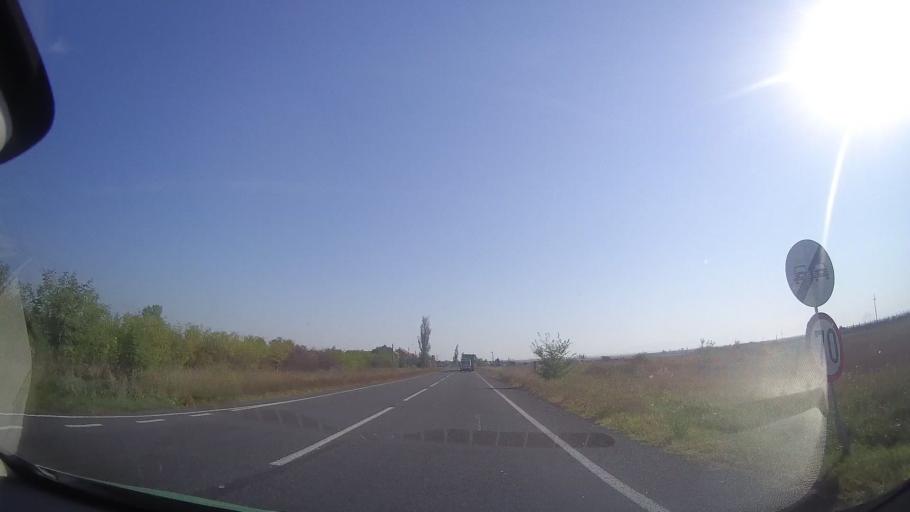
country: RO
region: Timis
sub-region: Comuna Topolovatu Mare
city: Topolovatu Mare
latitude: 45.7775
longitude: 21.6708
